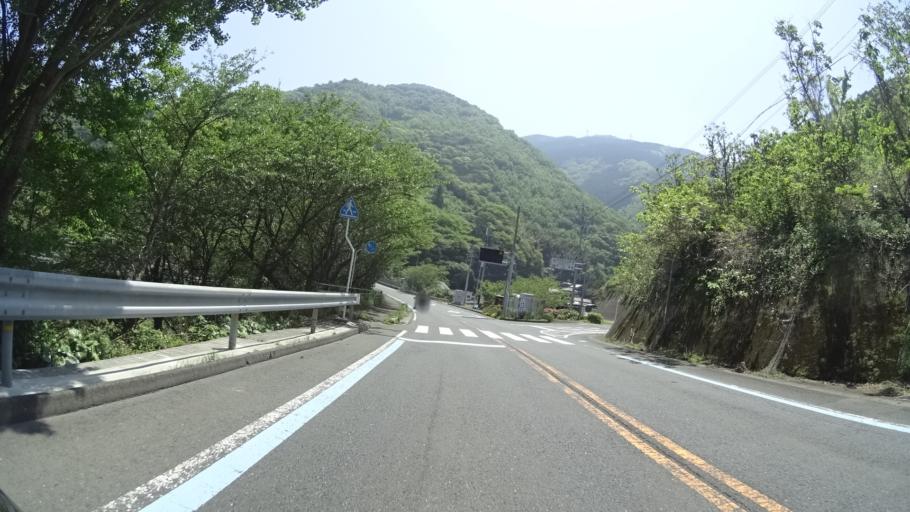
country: JP
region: Ehime
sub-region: Nishiuwa-gun
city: Ikata-cho
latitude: 33.5374
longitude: 132.4056
